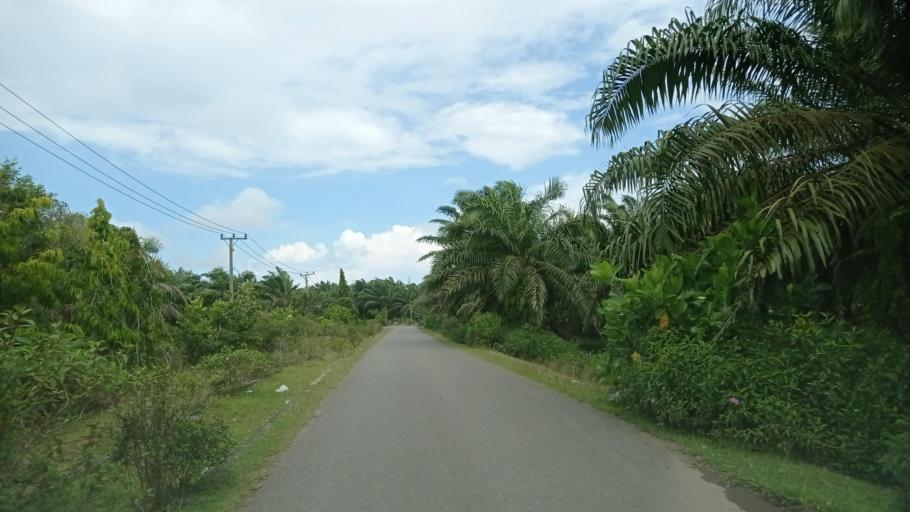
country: ID
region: Bengkulu
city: Ipuh
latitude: -2.5729
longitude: 101.1201
